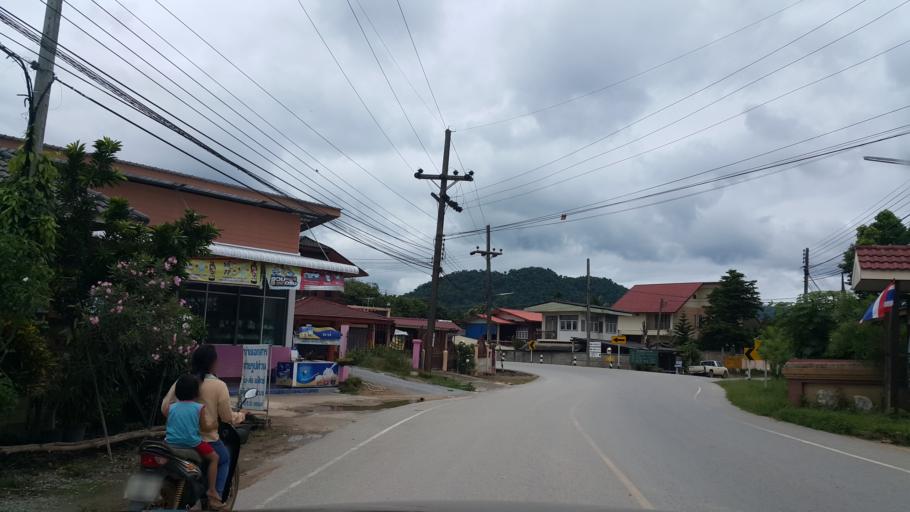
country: TH
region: Chiang Rai
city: Phaya Mengrai
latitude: 19.8918
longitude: 100.1085
